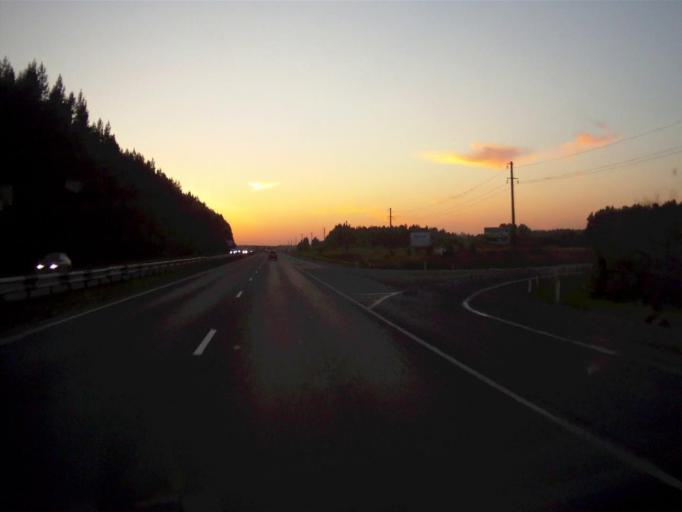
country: RU
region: Chelyabinsk
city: Roshchino
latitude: 55.1917
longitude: 61.2240
